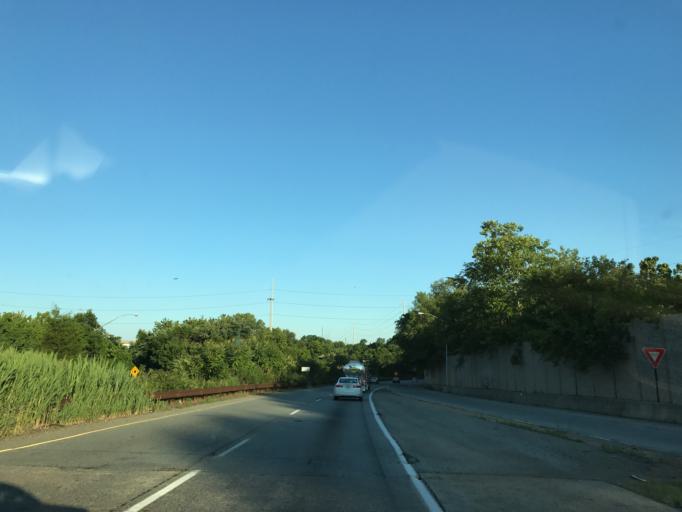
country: US
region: Pennsylvania
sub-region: Delaware County
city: Woodlyn
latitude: 39.8705
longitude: -75.3474
